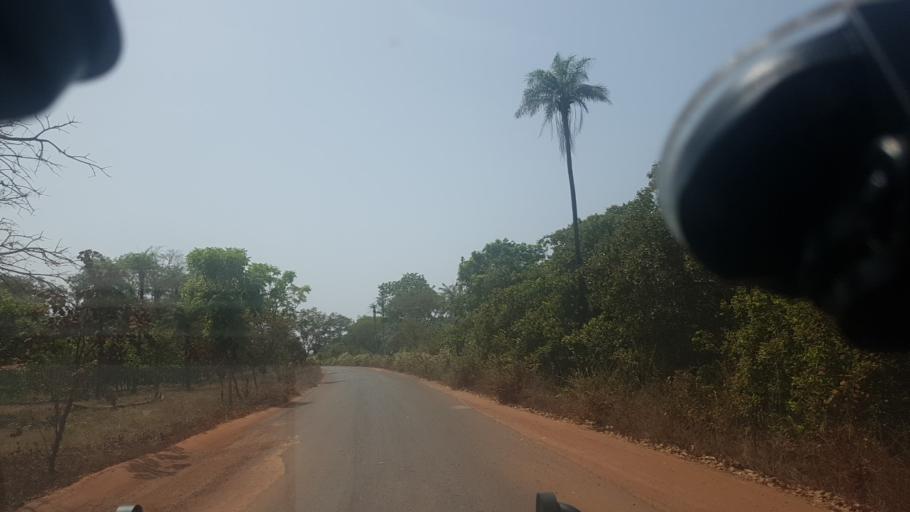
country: GW
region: Cacheu
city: Cacheu
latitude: 12.4098
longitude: -16.0303
